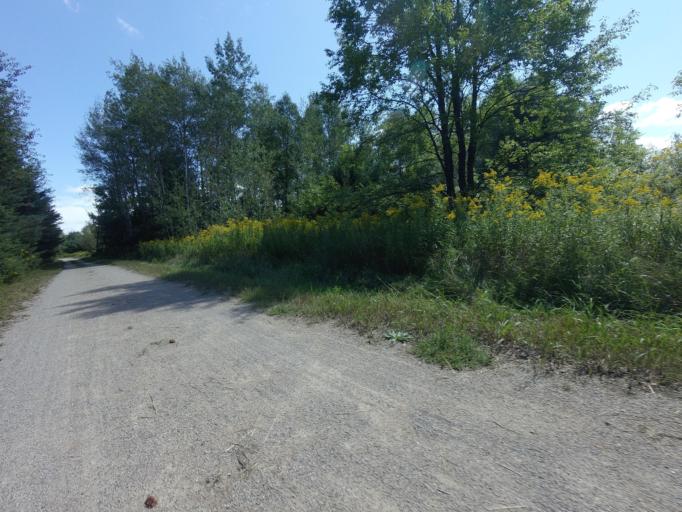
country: CA
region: Ontario
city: Orangeville
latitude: 43.7732
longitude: -80.1878
